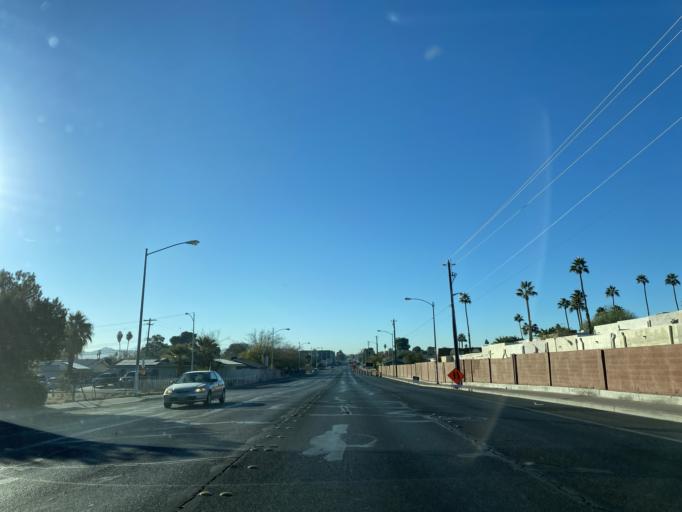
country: US
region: Nevada
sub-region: Clark County
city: Winchester
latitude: 36.1277
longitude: -115.0920
